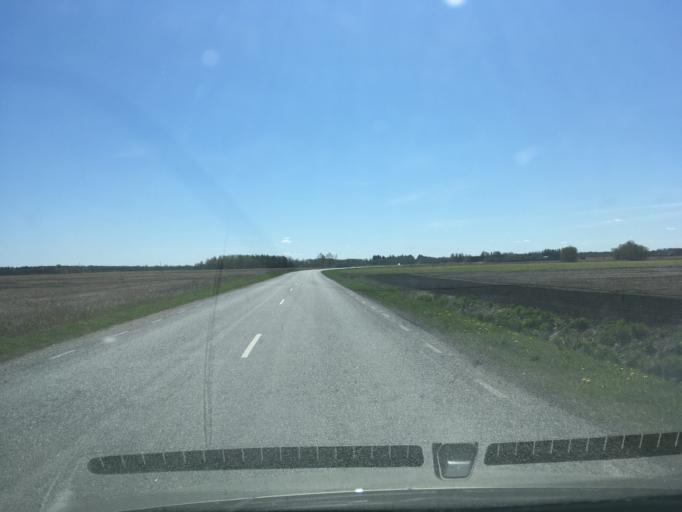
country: EE
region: Harju
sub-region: Raasiku vald
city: Arukula
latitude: 59.4206
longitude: 25.0776
